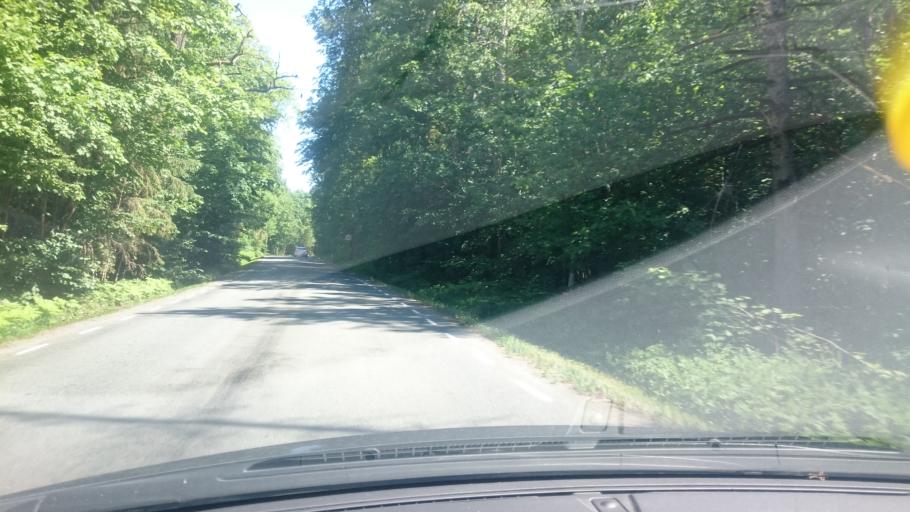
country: EE
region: Harju
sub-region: Rae vald
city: Vaida
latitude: 59.2056
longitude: 24.9306
